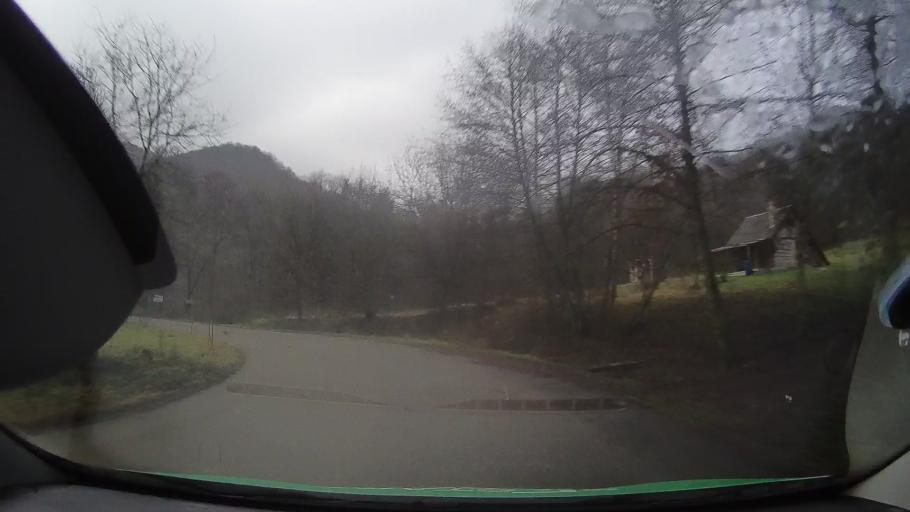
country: RO
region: Hunedoara
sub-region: Comuna Ribita
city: Ribita
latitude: 46.2519
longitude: 22.7497
